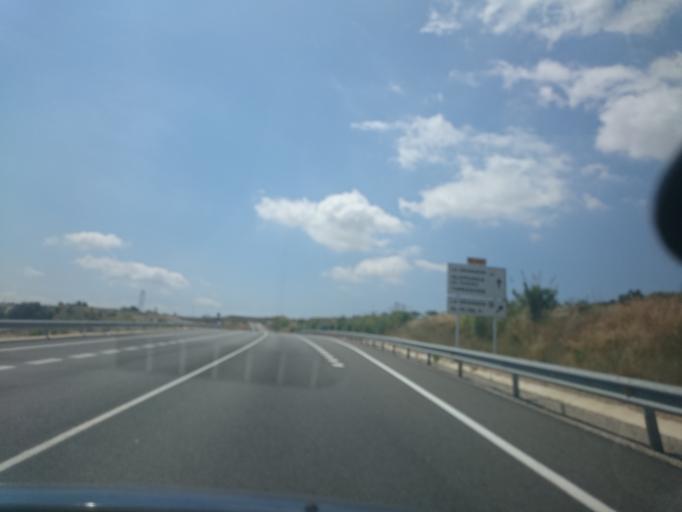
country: ES
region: Catalonia
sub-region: Provincia de Barcelona
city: La Granada
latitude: 41.3864
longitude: 1.7093
